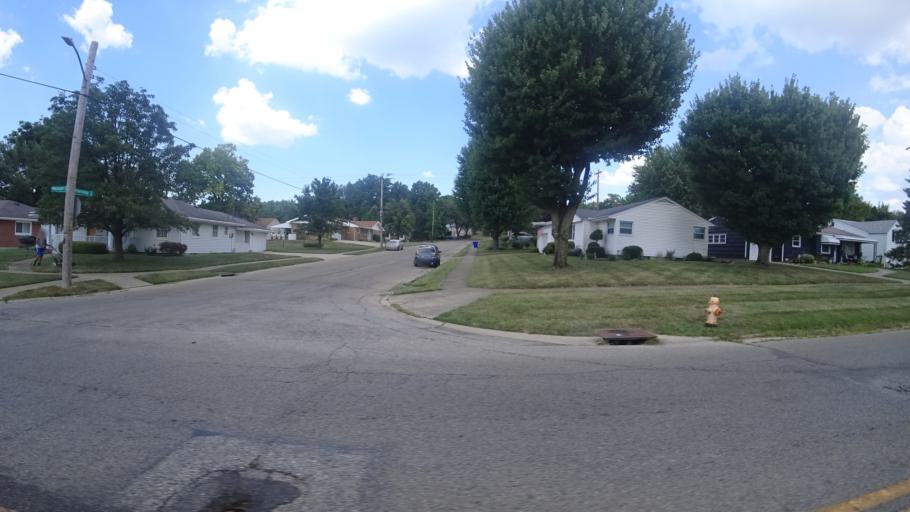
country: US
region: Ohio
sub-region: Butler County
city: Hamilton
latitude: 39.4247
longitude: -84.5706
